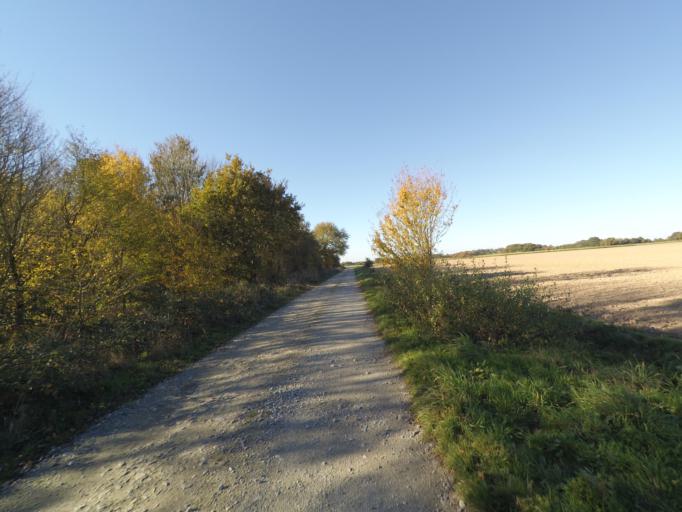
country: FR
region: Pays de la Loire
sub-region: Departement de la Loire-Atlantique
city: La Planche
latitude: 47.0212
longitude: -1.3957
